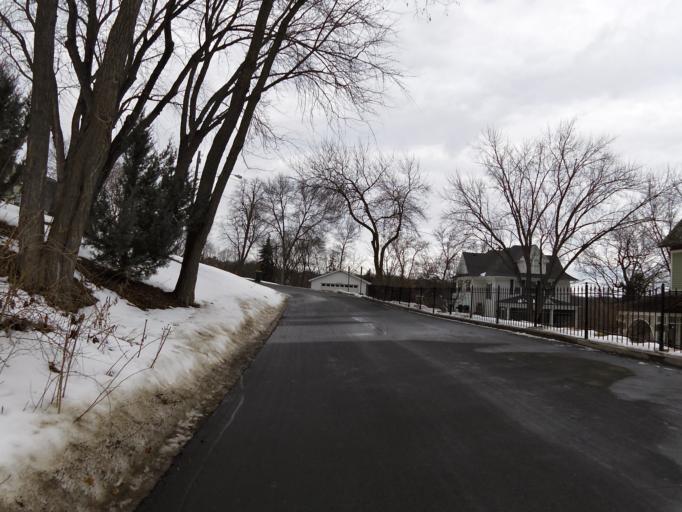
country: US
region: Minnesota
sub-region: Washington County
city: Stillwater
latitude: 45.0546
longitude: -92.8096
